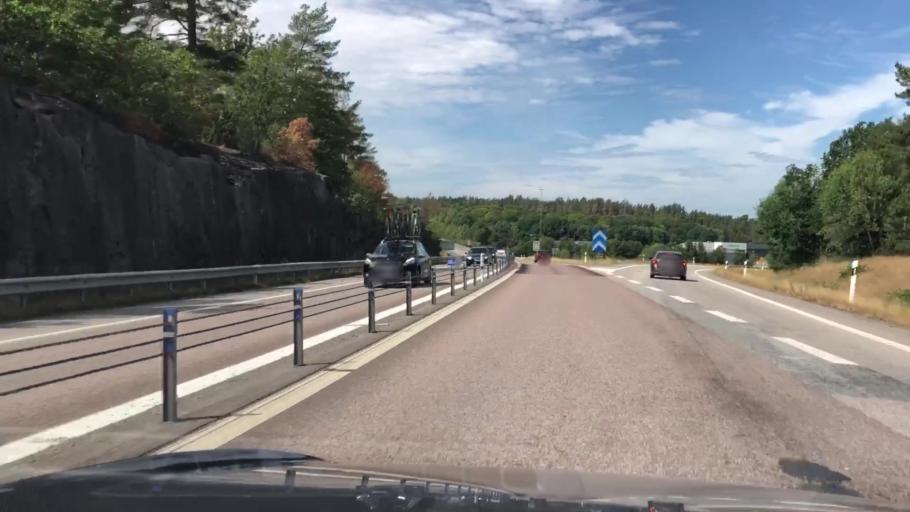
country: SE
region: Blekinge
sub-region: Ronneby Kommun
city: Kallinge
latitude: 56.2289
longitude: 15.2659
